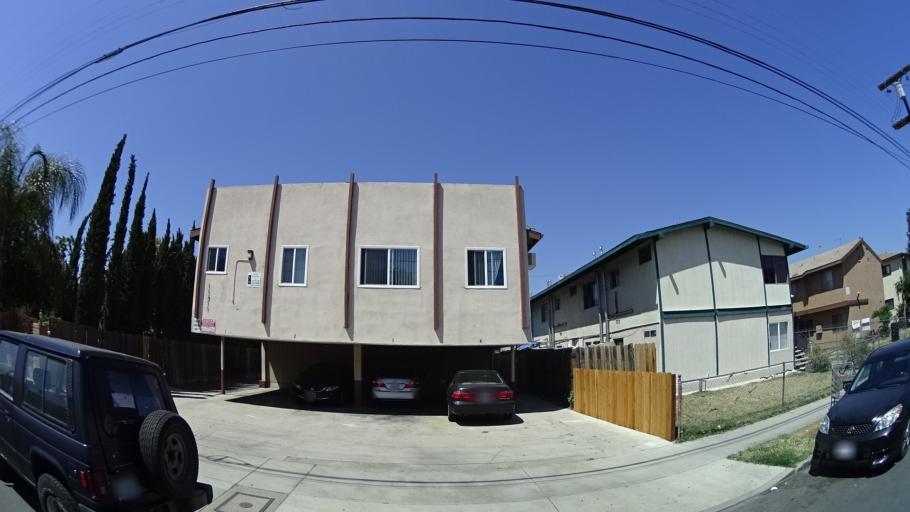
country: US
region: California
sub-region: Los Angeles County
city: North Hollywood
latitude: 34.1758
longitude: -118.3770
